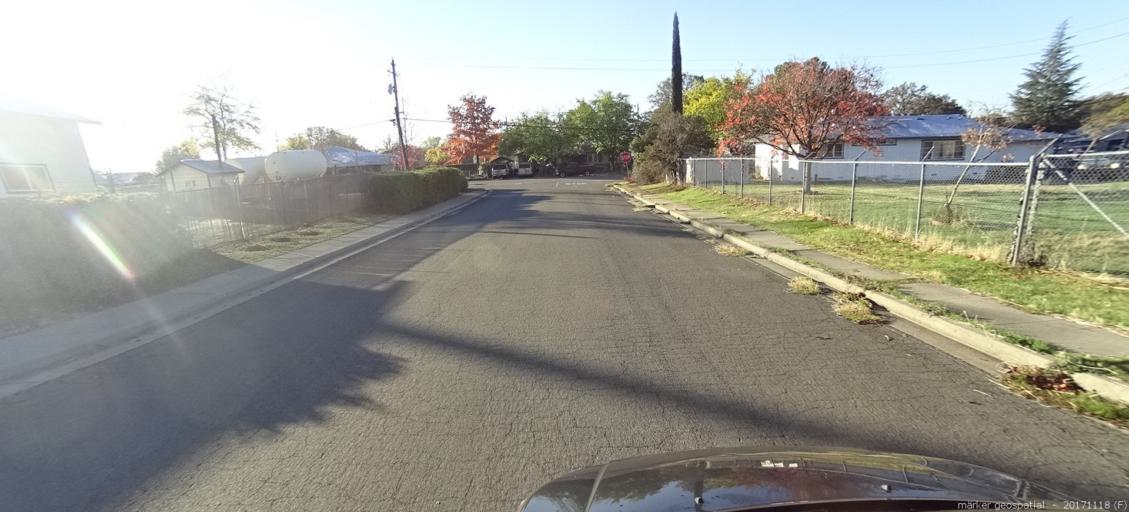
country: US
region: California
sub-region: Shasta County
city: Cottonwood
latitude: 40.3983
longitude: -122.2873
